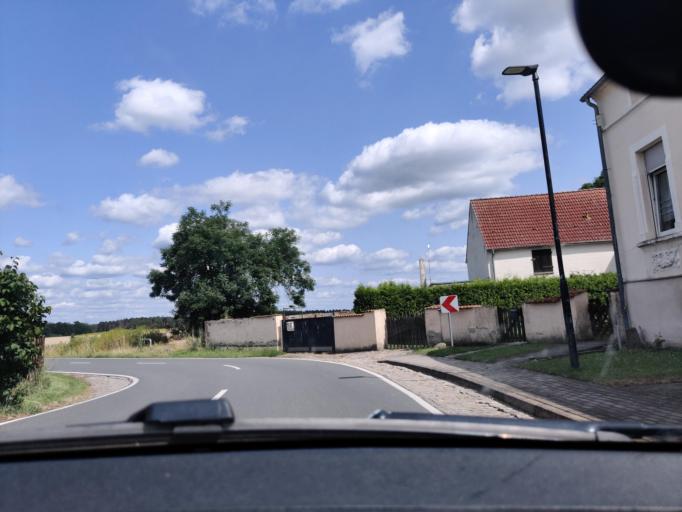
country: DE
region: Saxony-Anhalt
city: Loburg
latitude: 52.0773
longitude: 12.0453
